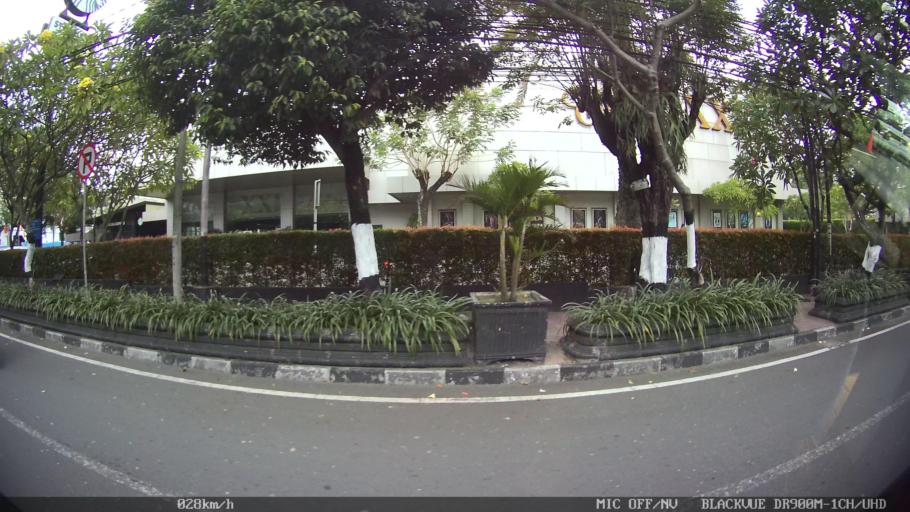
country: ID
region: Daerah Istimewa Yogyakarta
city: Yogyakarta
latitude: -7.7832
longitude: 110.3870
